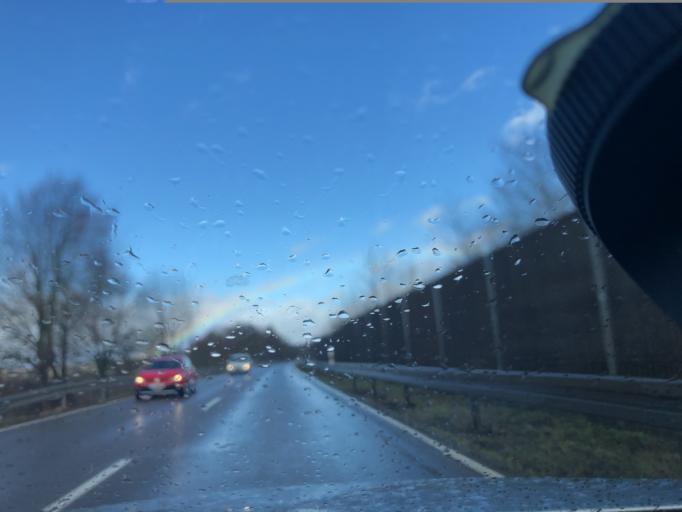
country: DE
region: Bavaria
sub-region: Upper Bavaria
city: Buxheim
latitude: 48.7788
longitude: 11.3217
